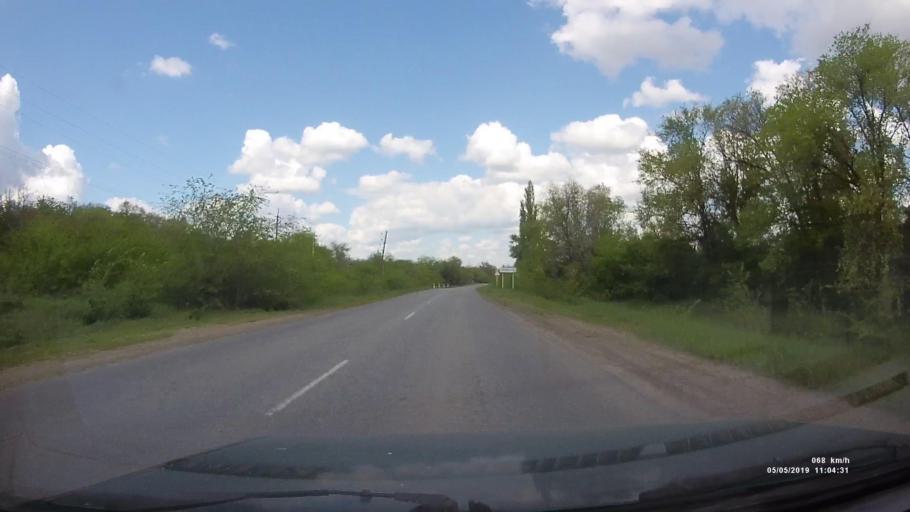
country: RU
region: Rostov
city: Ust'-Donetskiy
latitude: 47.6978
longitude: 40.9172
